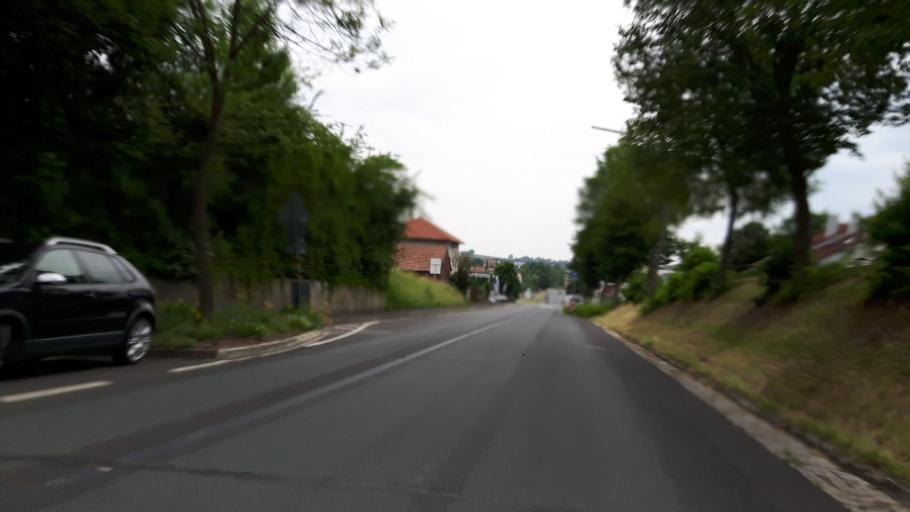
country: DE
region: Bavaria
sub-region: Regierungsbezirk Unterfranken
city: Estenfeld
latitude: 49.8312
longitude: 10.0055
